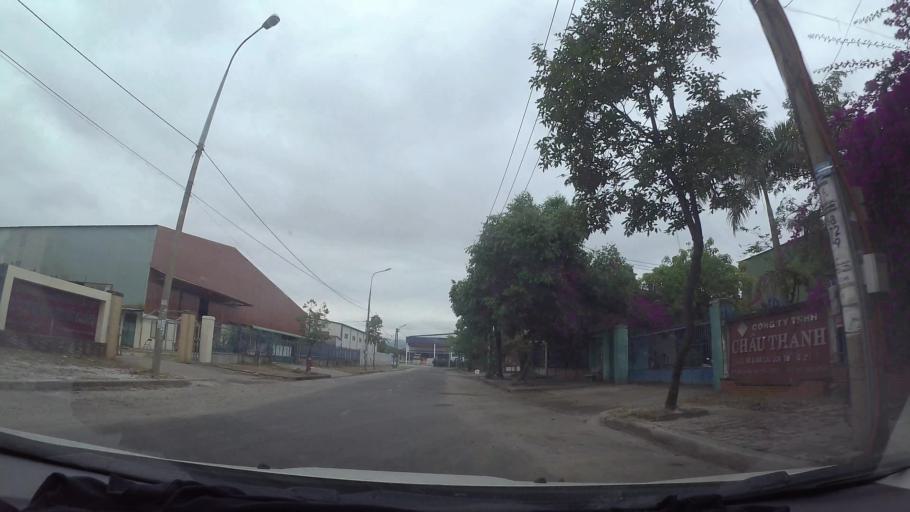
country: VN
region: Da Nang
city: Lien Chieu
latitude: 16.0868
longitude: 108.1376
